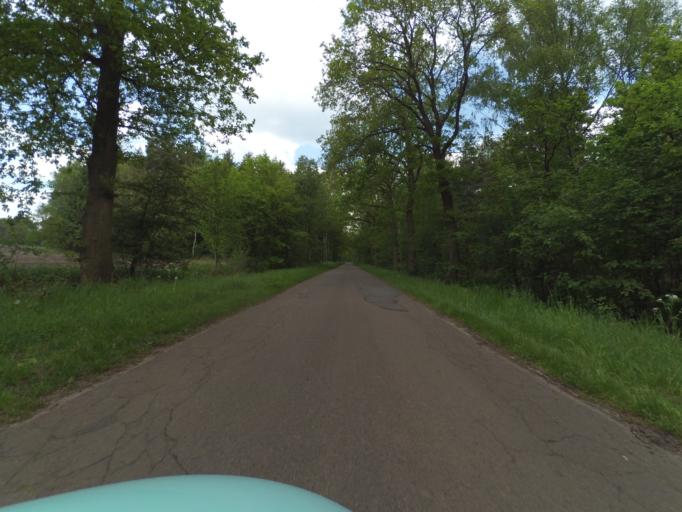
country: DE
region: Lower Saxony
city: Wietze
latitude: 52.5825
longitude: 9.8242
